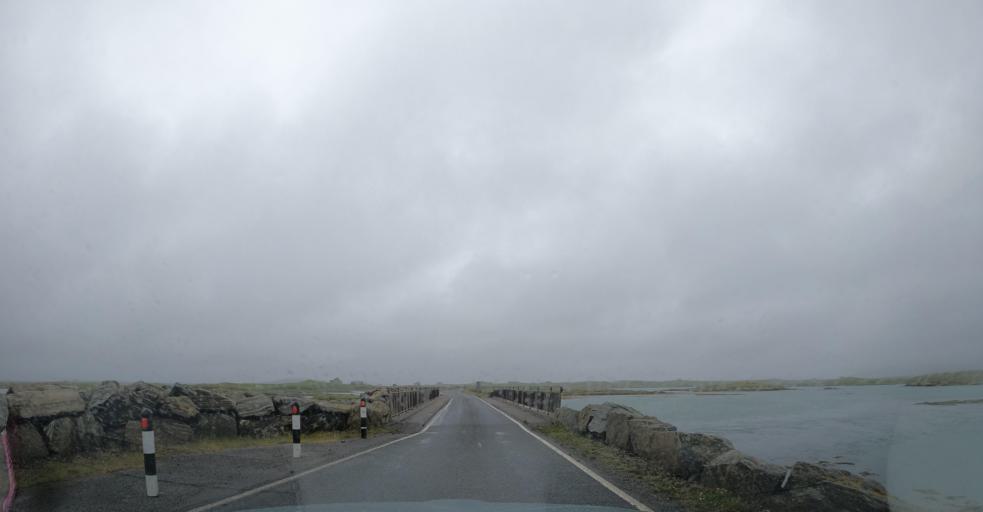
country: GB
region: Scotland
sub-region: Eilean Siar
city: Benbecula
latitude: 57.5026
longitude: -7.2631
